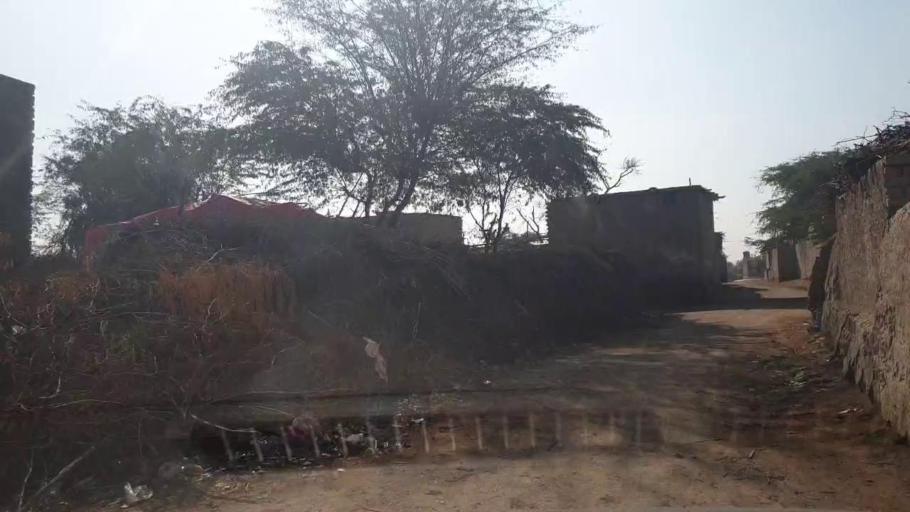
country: PK
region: Sindh
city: Shahdadpur
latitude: 25.9634
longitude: 68.5791
